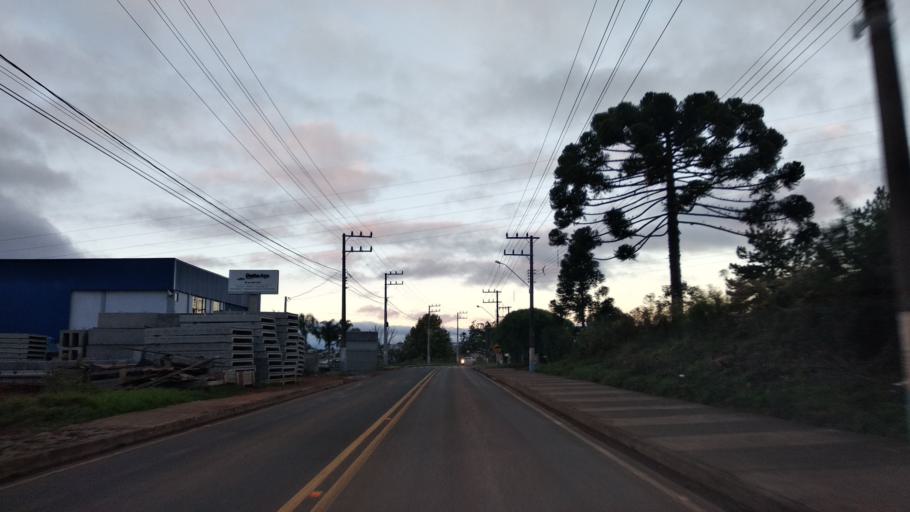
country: BR
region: Santa Catarina
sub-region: Campos Novos
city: Campos Novos
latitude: -27.3819
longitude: -51.2100
